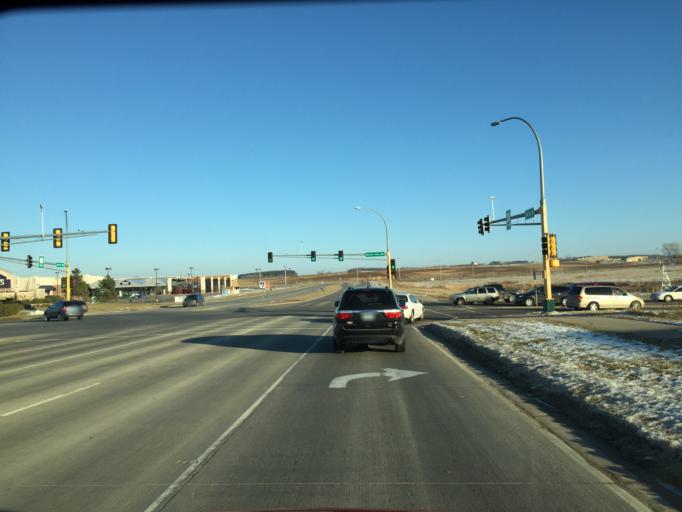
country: US
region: Minnesota
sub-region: Olmsted County
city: Rochester
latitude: 43.9529
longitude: -92.4633
